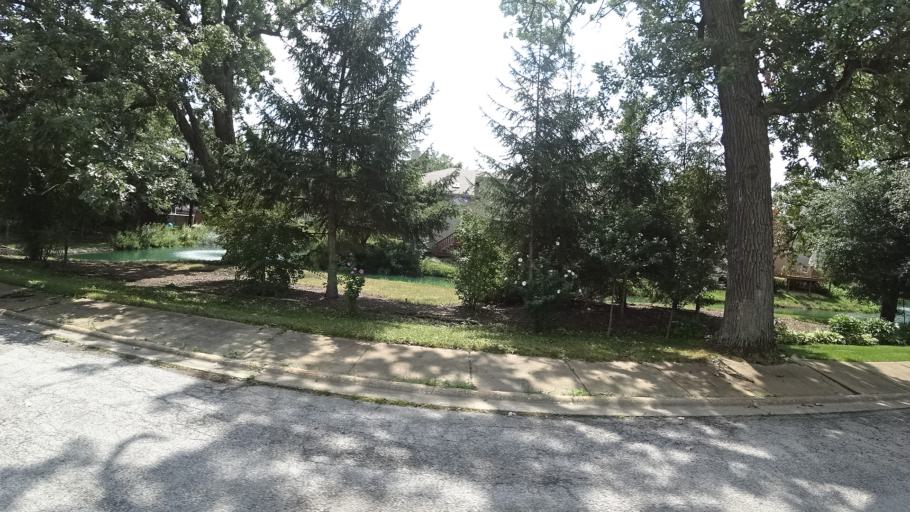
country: US
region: Illinois
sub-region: Cook County
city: Palos Heights
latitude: 41.6269
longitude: -87.7830
